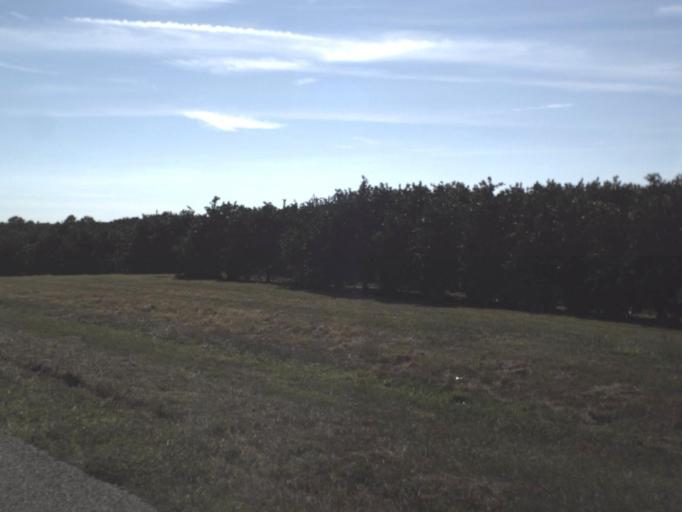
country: US
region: Florida
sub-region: Highlands County
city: Placid Lakes
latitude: 27.1194
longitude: -81.3311
